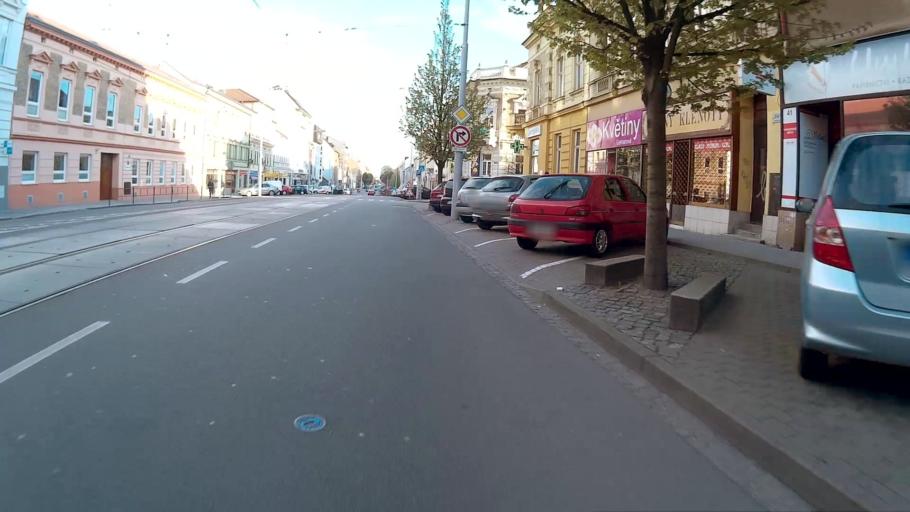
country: CZ
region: South Moravian
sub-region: Mesto Brno
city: Brno
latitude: 49.2226
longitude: 16.5956
